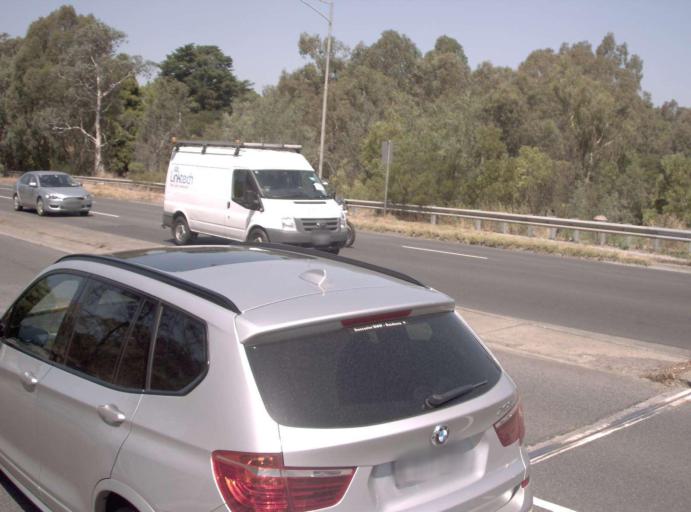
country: AU
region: Victoria
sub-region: Manningham
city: Bulleen
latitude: -37.7600
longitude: 145.0778
